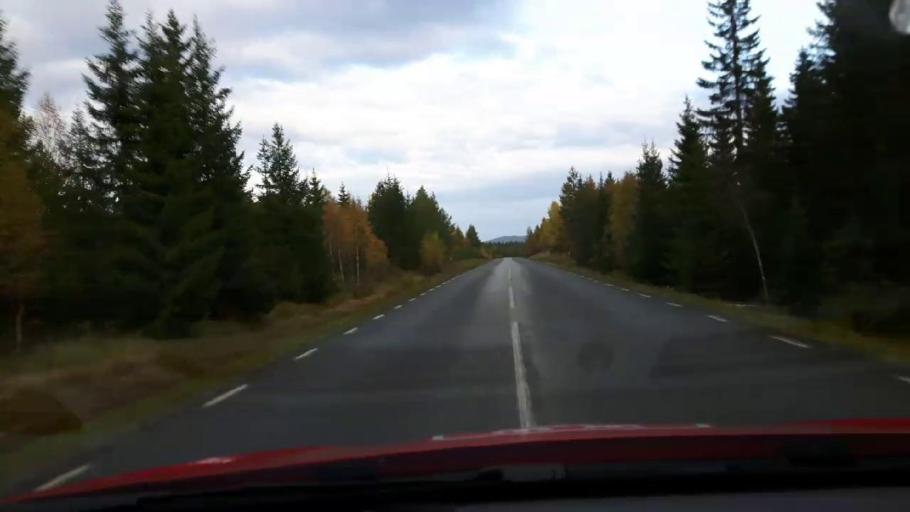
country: SE
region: Jaemtland
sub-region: OEstersunds Kommun
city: Ostersund
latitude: 63.3271
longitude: 14.6158
